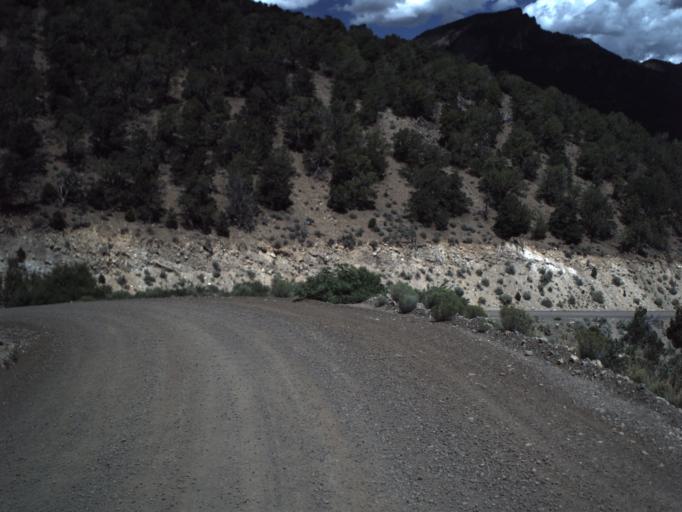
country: US
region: Utah
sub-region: Piute County
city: Junction
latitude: 38.2537
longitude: -112.3080
